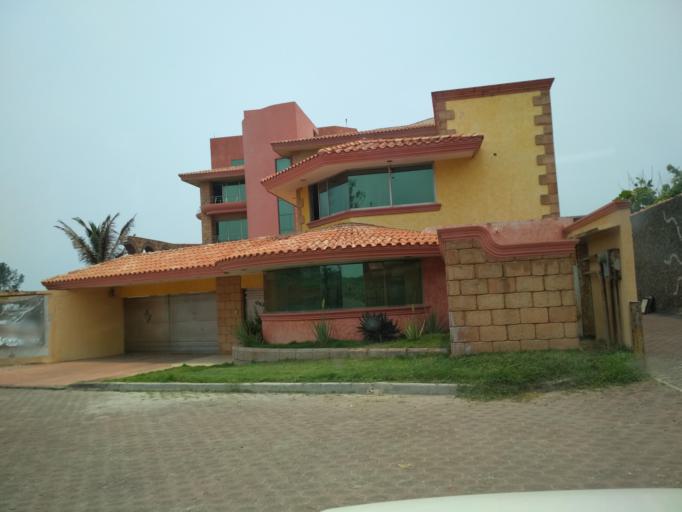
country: MX
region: Veracruz
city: Anton Lizardo
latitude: 19.0571
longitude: -96.0437
